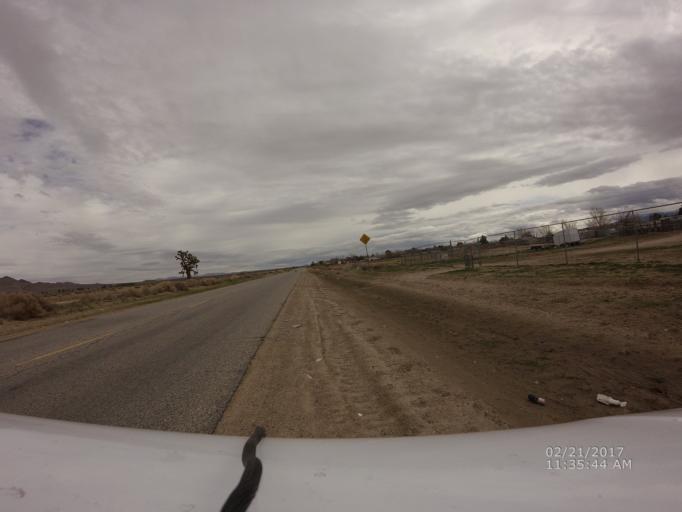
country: US
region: California
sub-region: Los Angeles County
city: Lake Los Angeles
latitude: 34.6312
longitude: -117.8393
